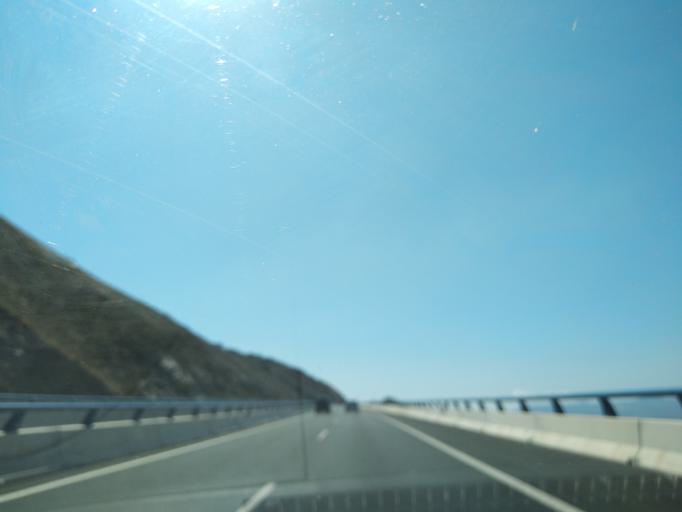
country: ES
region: Andalusia
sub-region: Provincia de Malaga
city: Almogia
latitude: 36.8538
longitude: -4.4850
